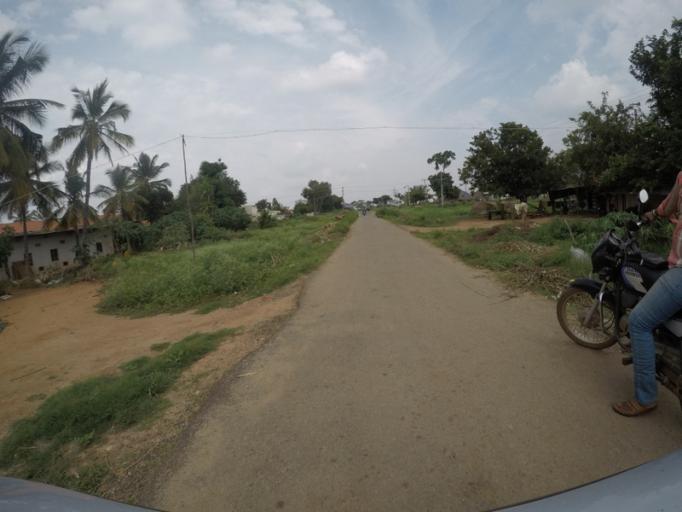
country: IN
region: Karnataka
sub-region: Mandya
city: Malavalli
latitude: 12.4145
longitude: 77.2265
